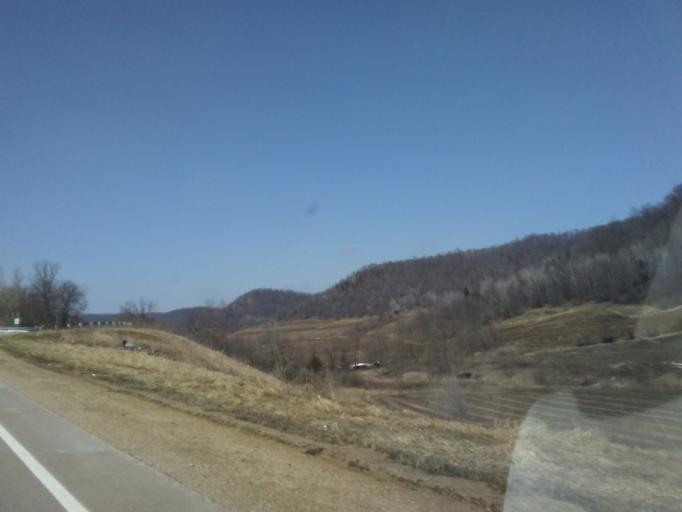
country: US
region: Wisconsin
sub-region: Vernon County
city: Westby
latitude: 43.7037
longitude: -91.0452
